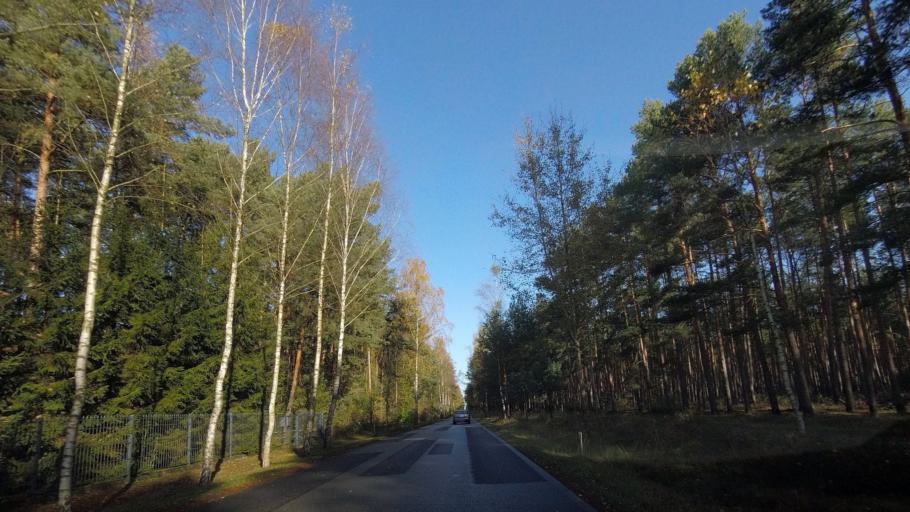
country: DE
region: Brandenburg
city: Borkwalde
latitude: 52.2709
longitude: 12.8344
